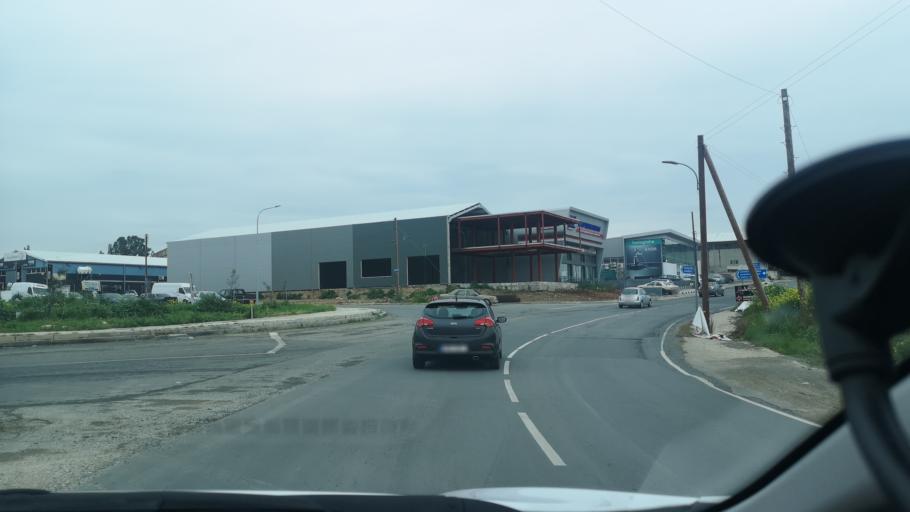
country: CY
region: Lefkosia
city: Tseri
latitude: 35.1038
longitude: 33.3321
